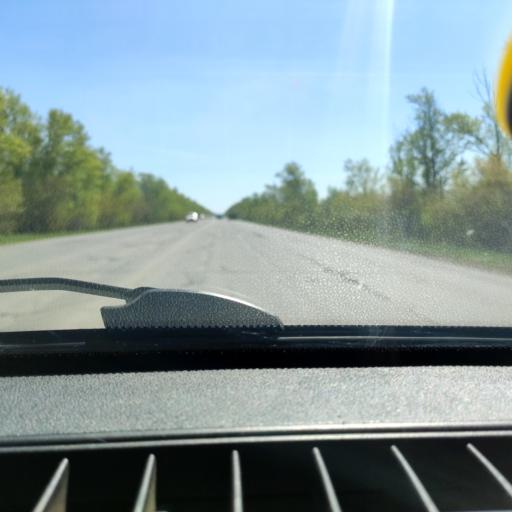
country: RU
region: Samara
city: Tol'yatti
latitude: 53.6090
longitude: 49.4113
